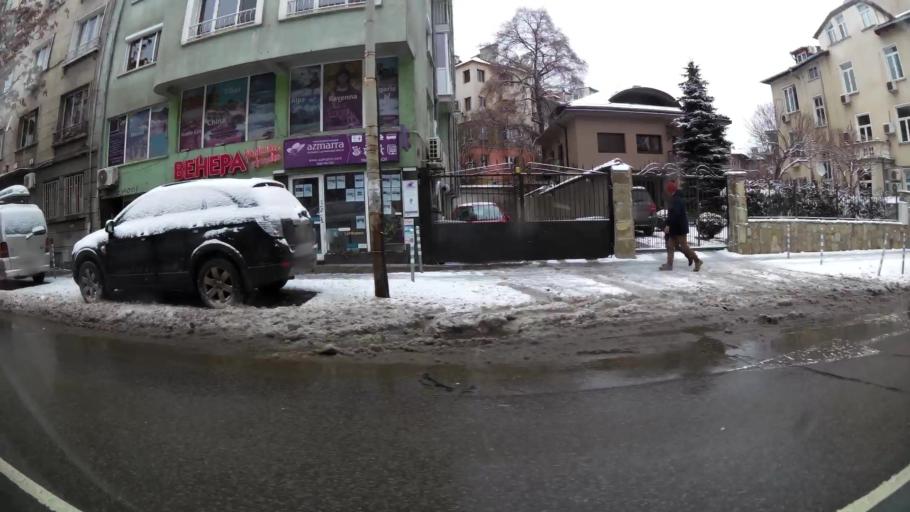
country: BG
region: Sofia-Capital
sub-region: Stolichna Obshtina
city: Sofia
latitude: 42.6928
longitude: 23.3445
